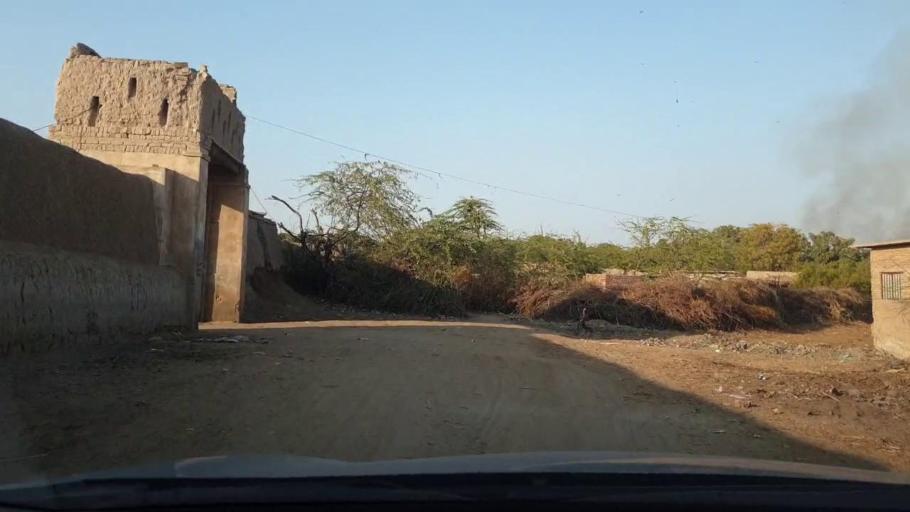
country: PK
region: Sindh
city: Berani
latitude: 25.6360
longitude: 68.8102
